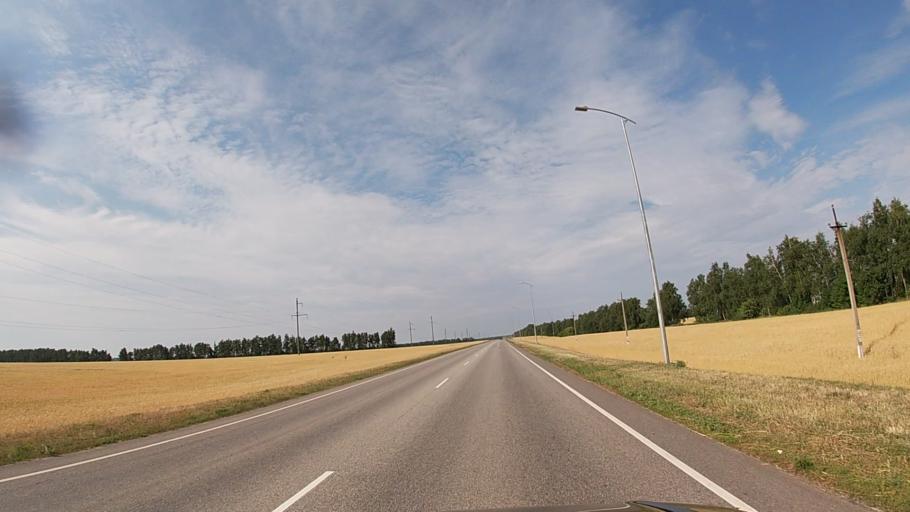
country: RU
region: Belgorod
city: Proletarskiy
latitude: 50.8242
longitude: 35.7593
